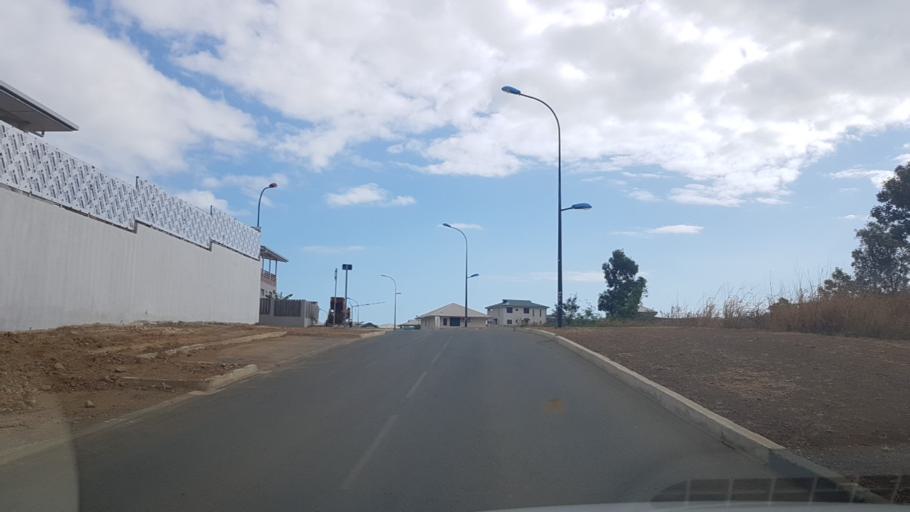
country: NC
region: South Province
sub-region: Dumbea
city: Dumbea
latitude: -22.1987
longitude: 166.4420
